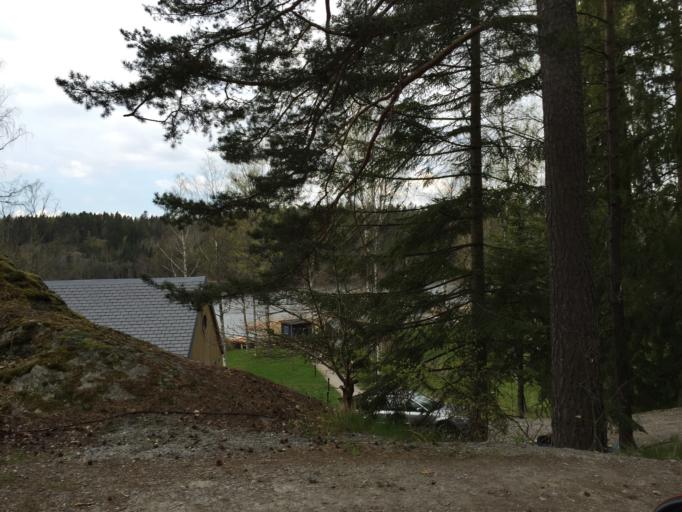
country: SE
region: Stockholm
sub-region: Salems Kommun
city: Ronninge
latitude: 59.1908
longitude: 17.7119
